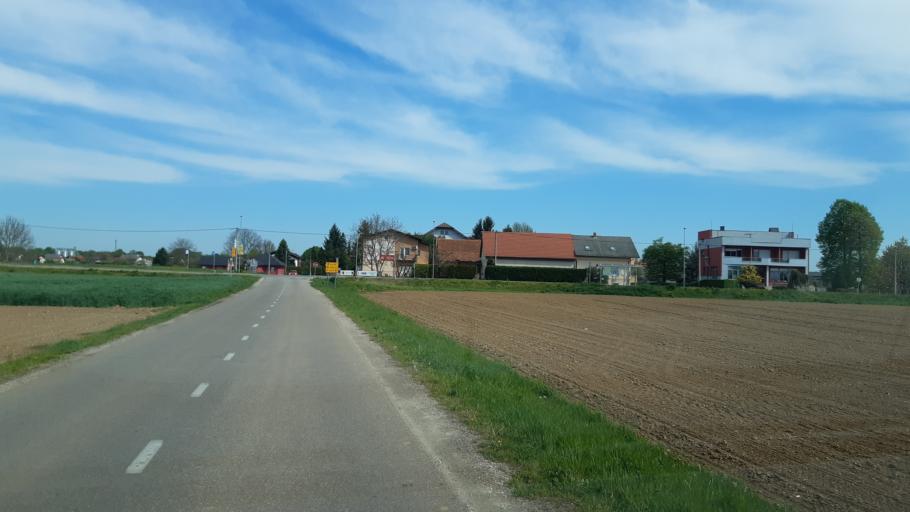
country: SI
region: Murska Sobota
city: Cernelavci
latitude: 46.6636
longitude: 16.1364
